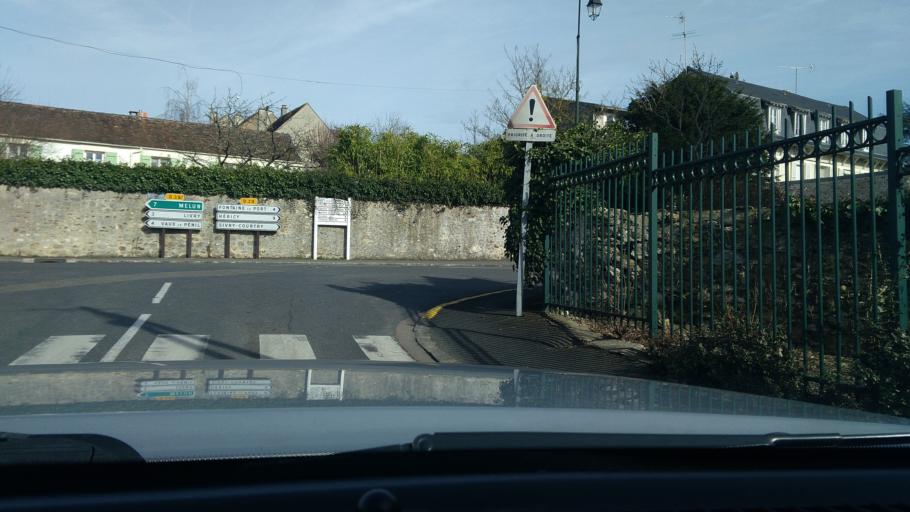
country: FR
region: Ile-de-France
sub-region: Departement de Seine-et-Marne
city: Chartrettes
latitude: 48.4888
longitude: 2.6981
